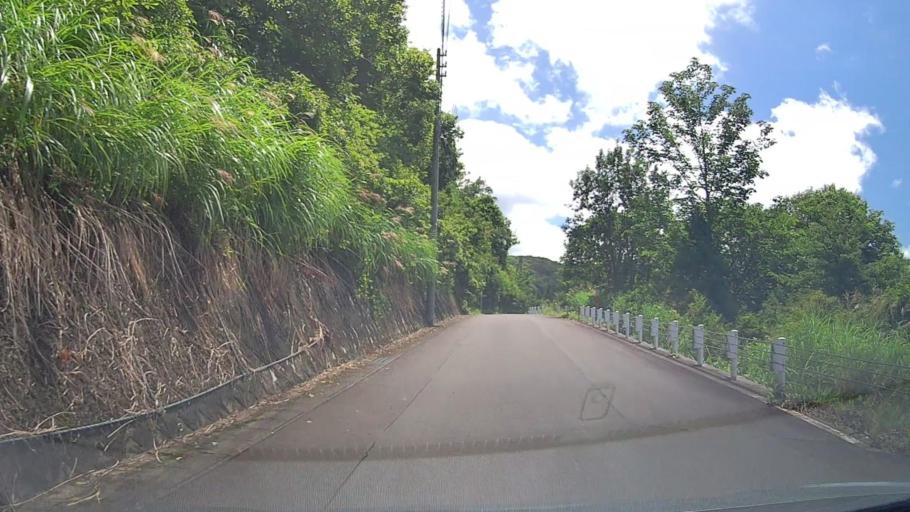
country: JP
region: Nagano
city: Iiyama
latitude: 36.9350
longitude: 138.4639
